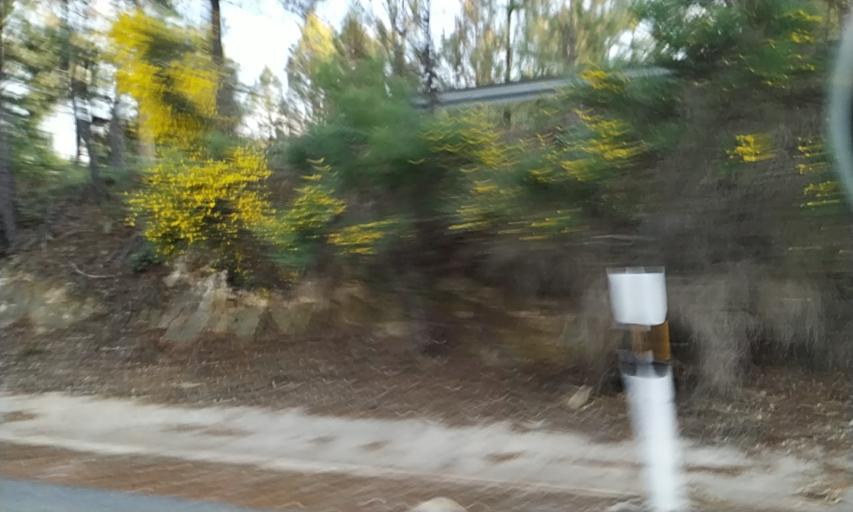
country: PT
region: Portalegre
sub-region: Portalegre
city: Sao Juliao
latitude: 39.3428
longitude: -7.2925
